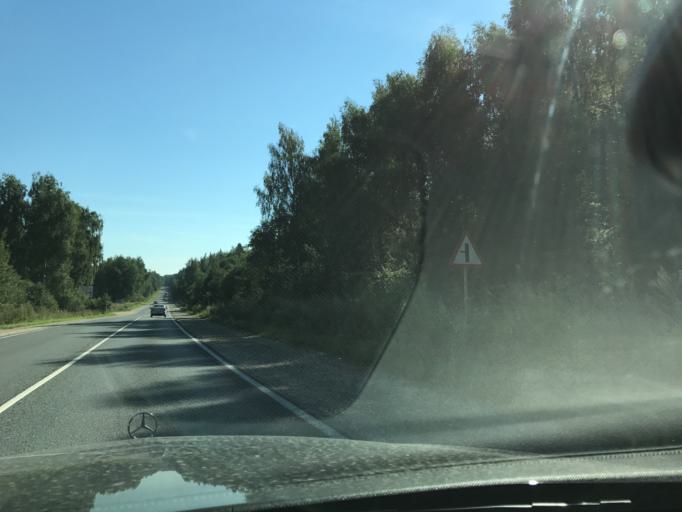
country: RU
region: Vladimir
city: Kirzhach
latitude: 56.1350
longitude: 38.7898
